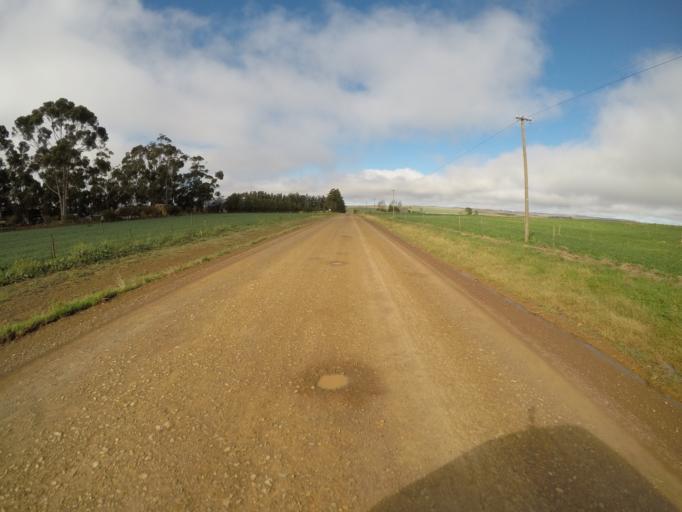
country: ZA
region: Western Cape
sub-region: Cape Winelands District Municipality
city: Ashton
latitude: -34.1402
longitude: 19.8623
